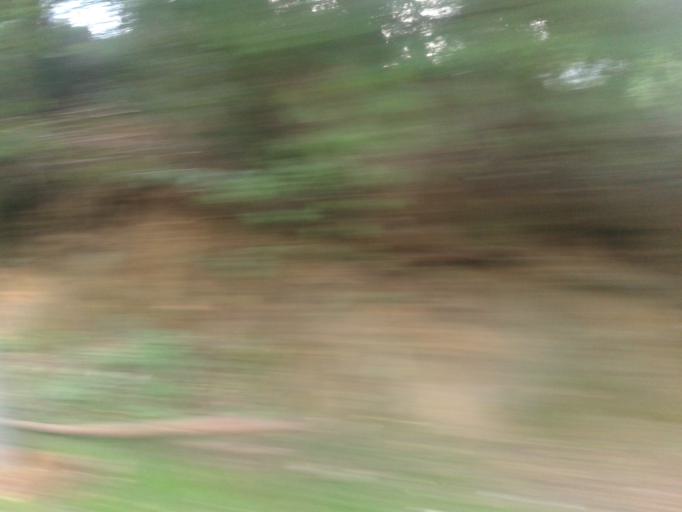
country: IN
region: Tamil Nadu
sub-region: Dindigul
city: Kodaikanal
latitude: 10.2314
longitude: 77.4831
